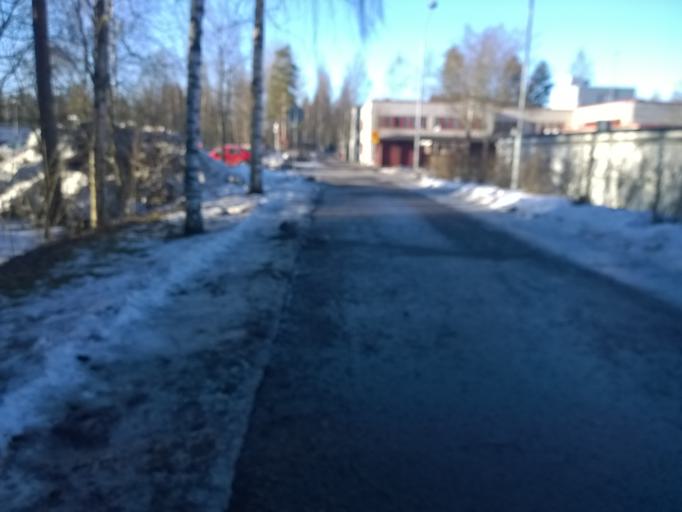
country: FI
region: Pirkanmaa
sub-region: Tampere
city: Tampere
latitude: 61.4460
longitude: 23.8315
